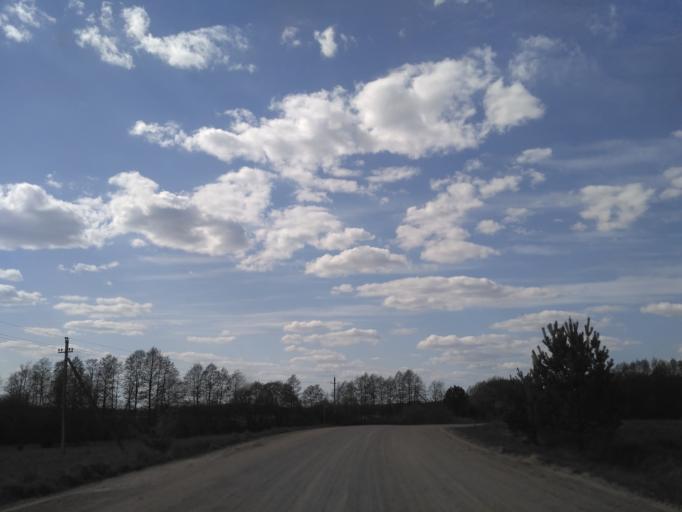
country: BY
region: Minsk
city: Narach
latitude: 54.9945
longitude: 26.5616
